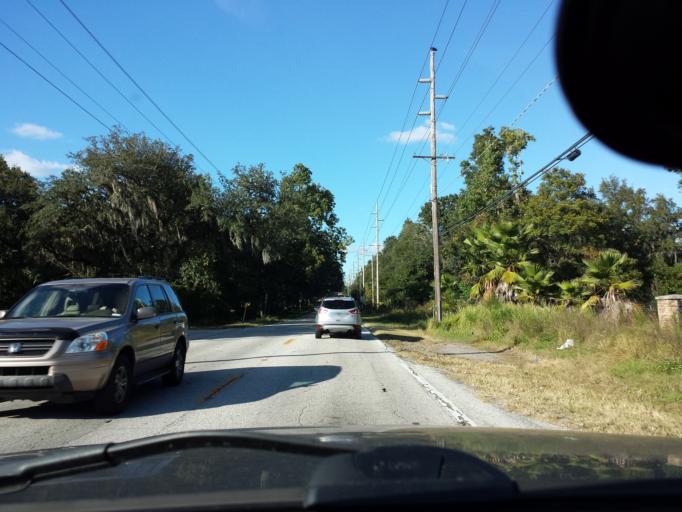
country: US
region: Florida
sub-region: Hillsborough County
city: Bloomingdale
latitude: 27.8618
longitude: -82.2692
